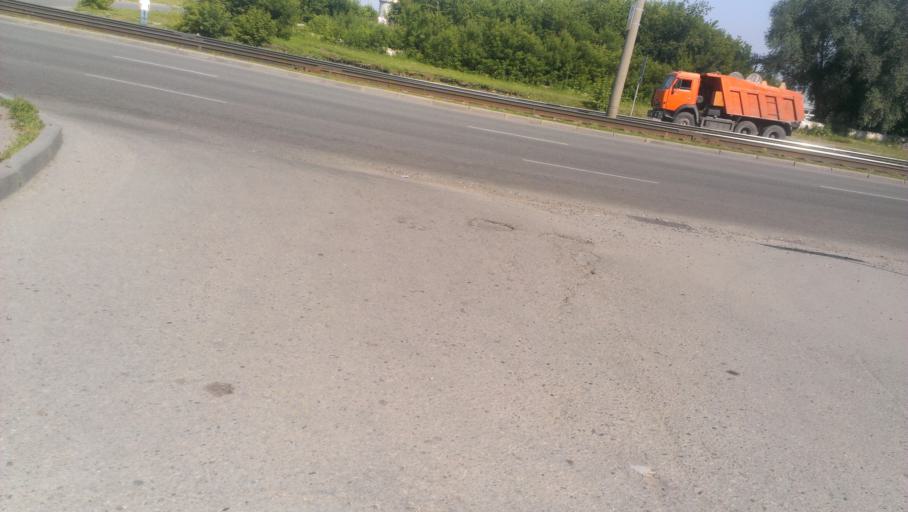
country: RU
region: Altai Krai
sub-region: Gorod Barnaulskiy
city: Barnaul
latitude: 53.3817
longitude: 83.6832
